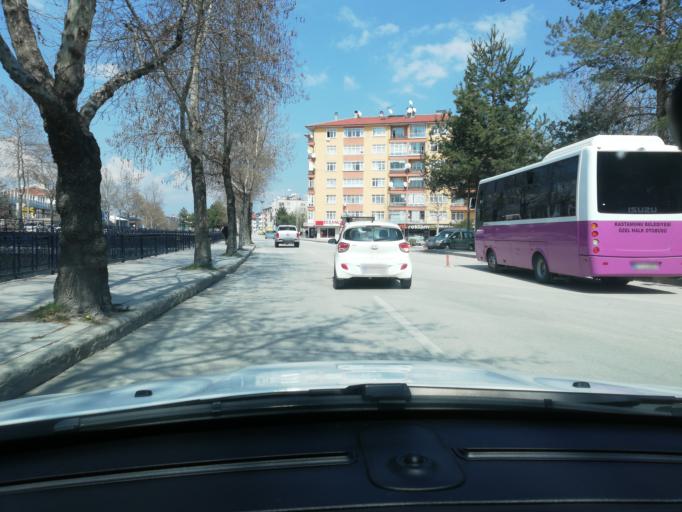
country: TR
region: Kastamonu
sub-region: Cide
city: Kastamonu
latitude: 41.3901
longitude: 33.7814
